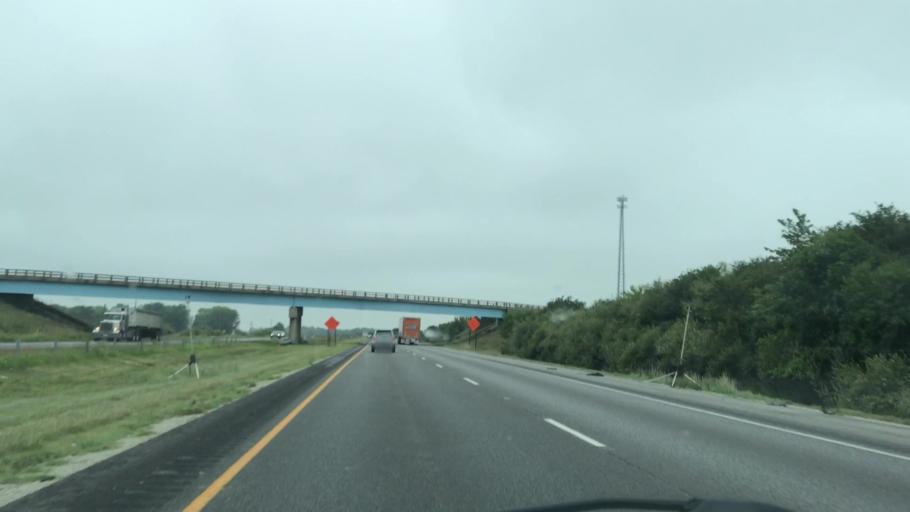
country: US
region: Indiana
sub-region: Boone County
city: Thorntown
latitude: 40.1959
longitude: -86.5723
